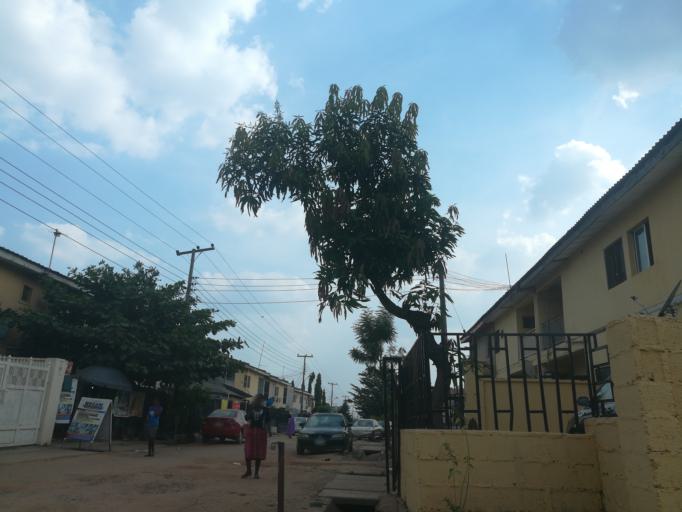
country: NG
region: Abuja Federal Capital Territory
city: Abuja
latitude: 9.0828
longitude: 7.4131
